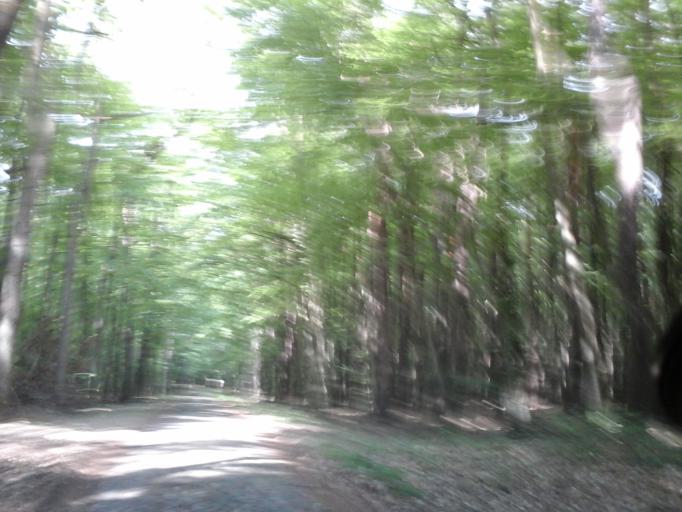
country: PL
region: West Pomeranian Voivodeship
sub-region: Powiat choszczenski
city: Drawno
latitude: 53.1046
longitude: 15.8872
